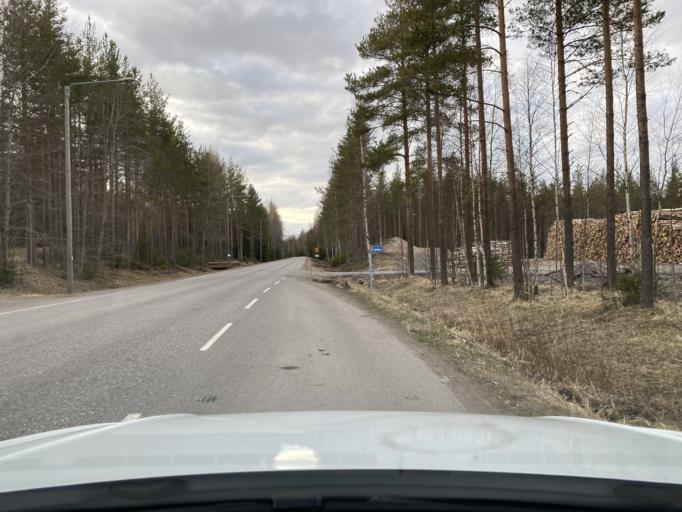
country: FI
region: Uusimaa
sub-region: Helsinki
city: Kaerkoelae
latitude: 60.8287
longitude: 24.0163
